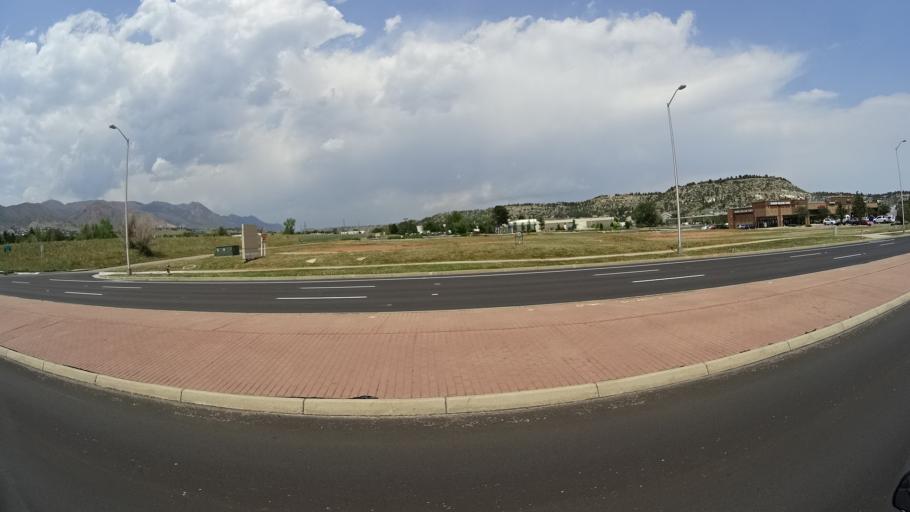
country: US
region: Colorado
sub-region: El Paso County
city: Manitou Springs
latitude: 38.8965
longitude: -104.8564
